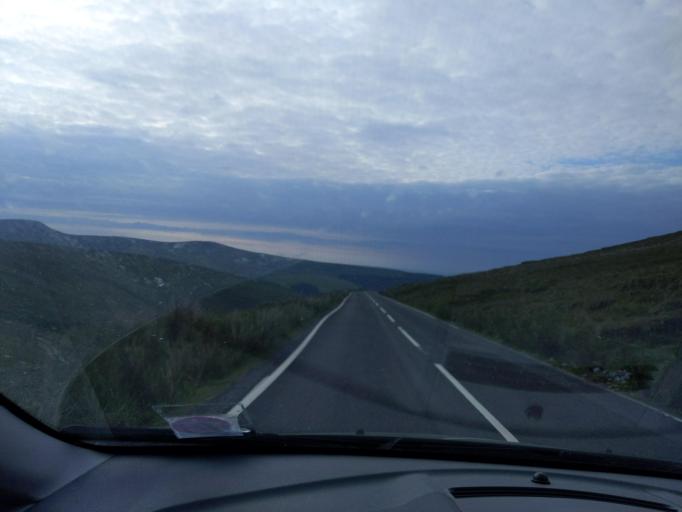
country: IM
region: Laxey
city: Laxey
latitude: 54.2546
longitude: -4.4719
